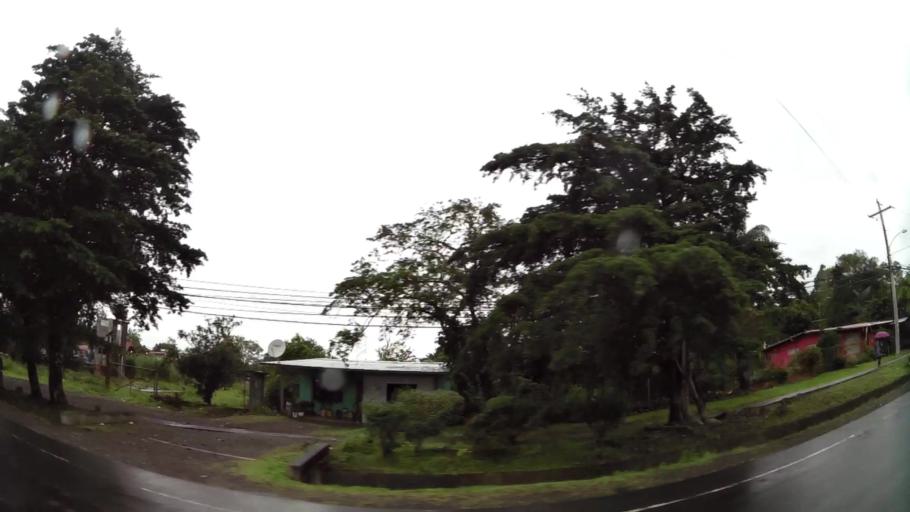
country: PA
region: Chiriqui
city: Volcan
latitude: 8.7769
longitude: -82.6401
